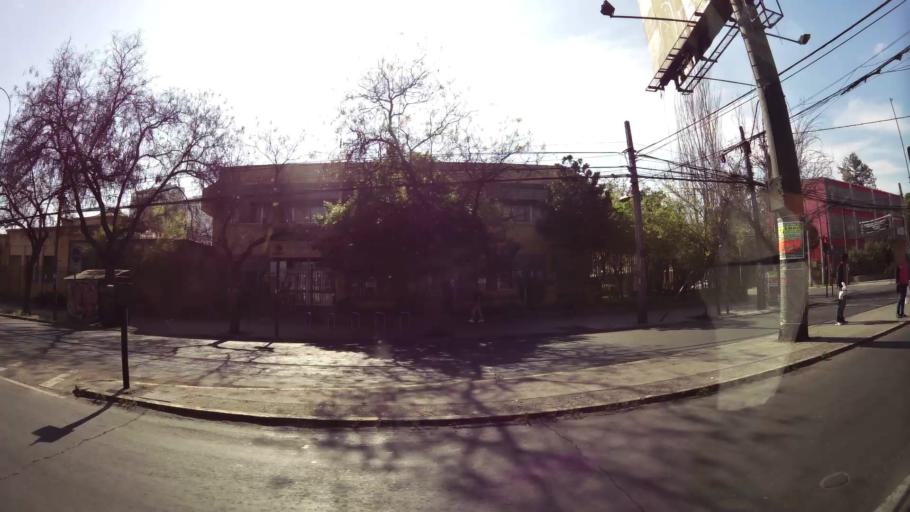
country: CL
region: Santiago Metropolitan
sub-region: Provincia de Santiago
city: Santiago
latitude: -33.4155
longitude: -70.6573
